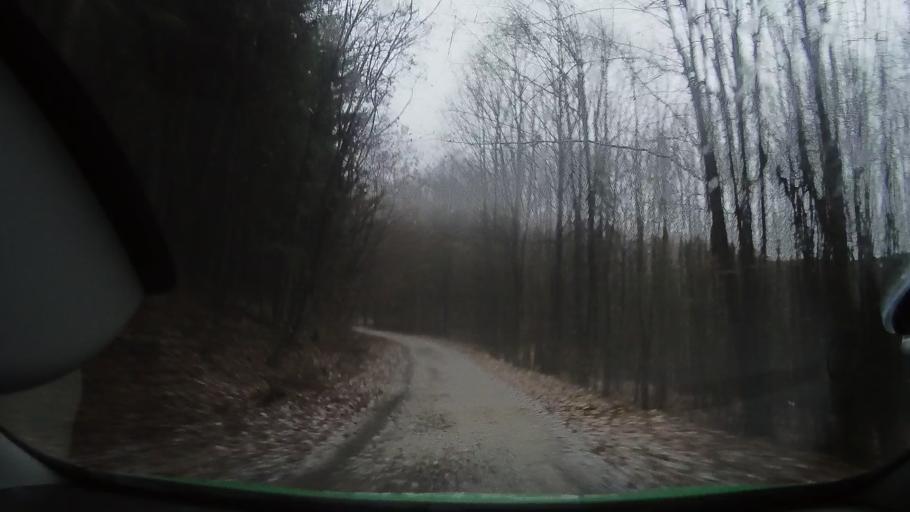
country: RO
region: Alba
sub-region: Comuna Avram Iancu
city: Avram Iancu
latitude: 46.3124
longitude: 22.7937
